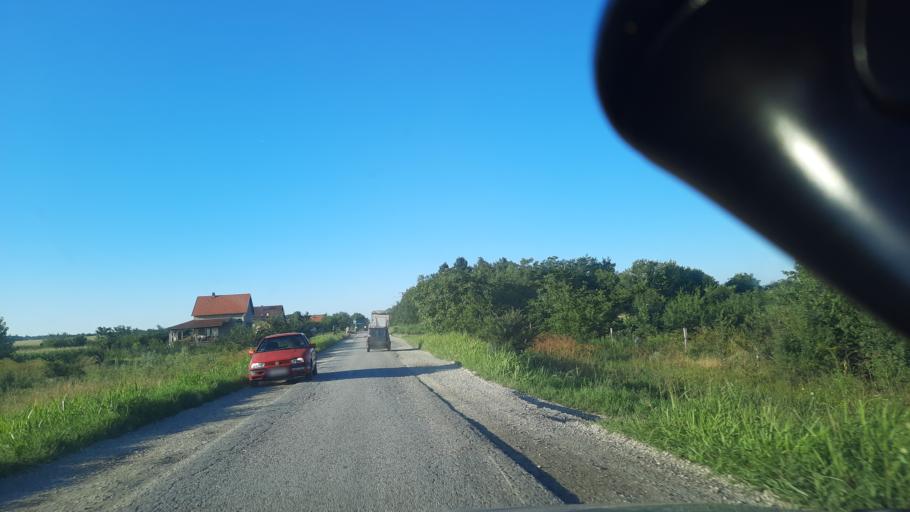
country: RS
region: Autonomna Pokrajina Vojvodina
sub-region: Sremski Okrug
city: Irig
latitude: 45.1102
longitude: 19.9319
